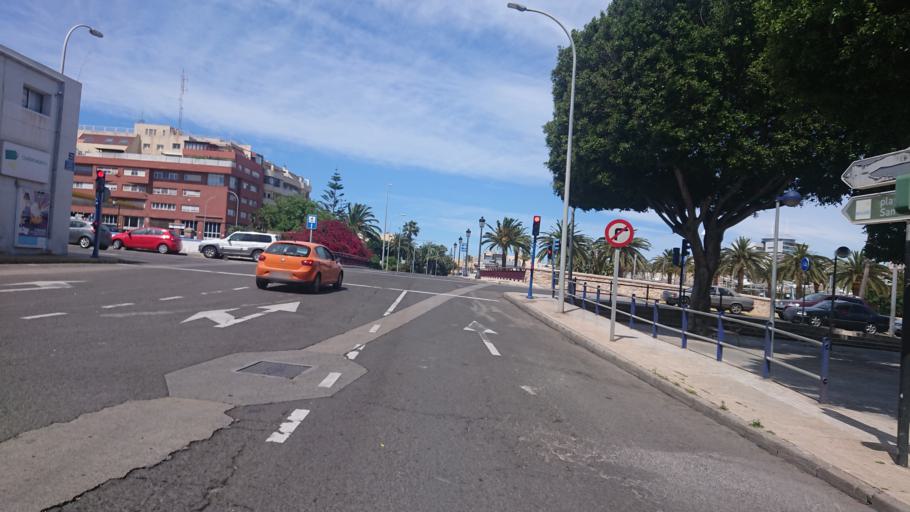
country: ES
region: Melilla
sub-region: Melilla
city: Melilla
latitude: 35.2862
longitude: -2.9415
